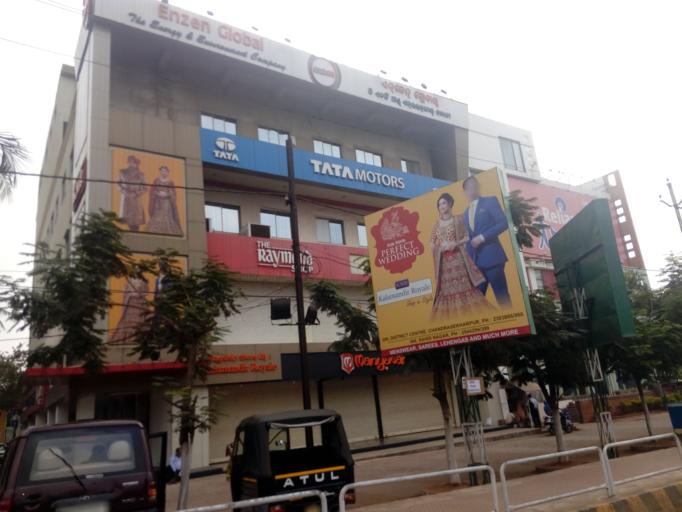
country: IN
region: Odisha
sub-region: Khordha
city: Bhubaneshwar
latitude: 20.2887
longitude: 85.8430
